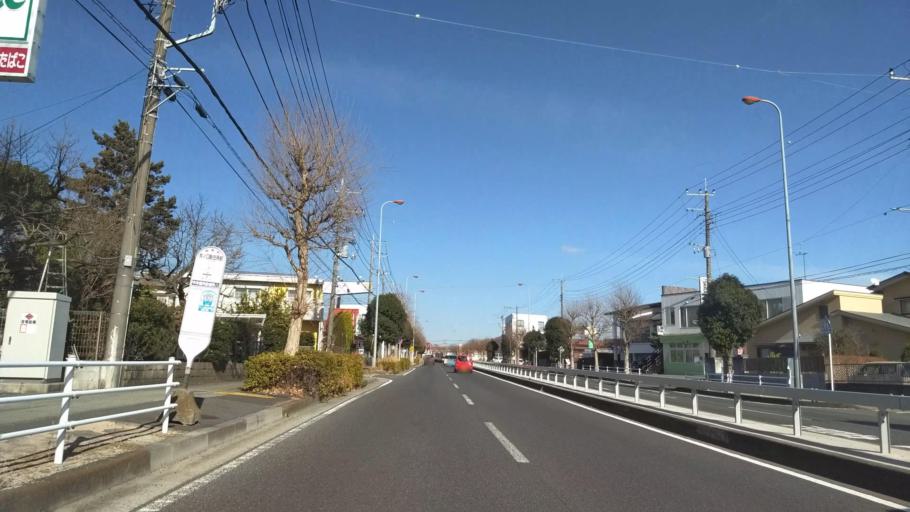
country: JP
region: Kanagawa
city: Hadano
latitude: 35.3469
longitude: 139.2327
